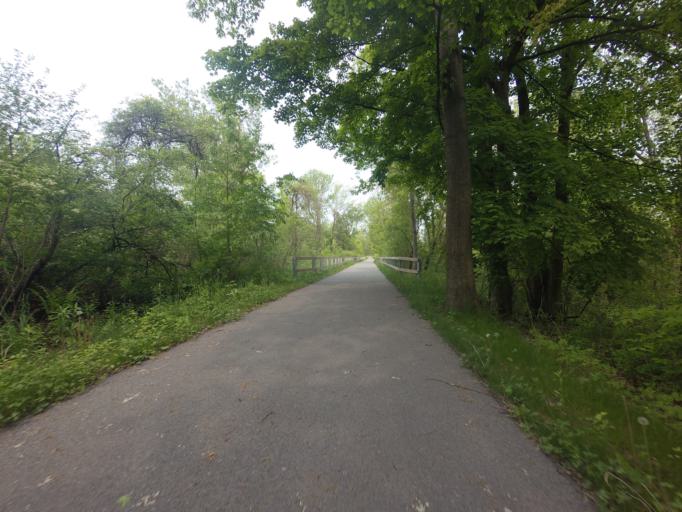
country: US
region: New York
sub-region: Jefferson County
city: Watertown
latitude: 43.9717
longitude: -75.8712
